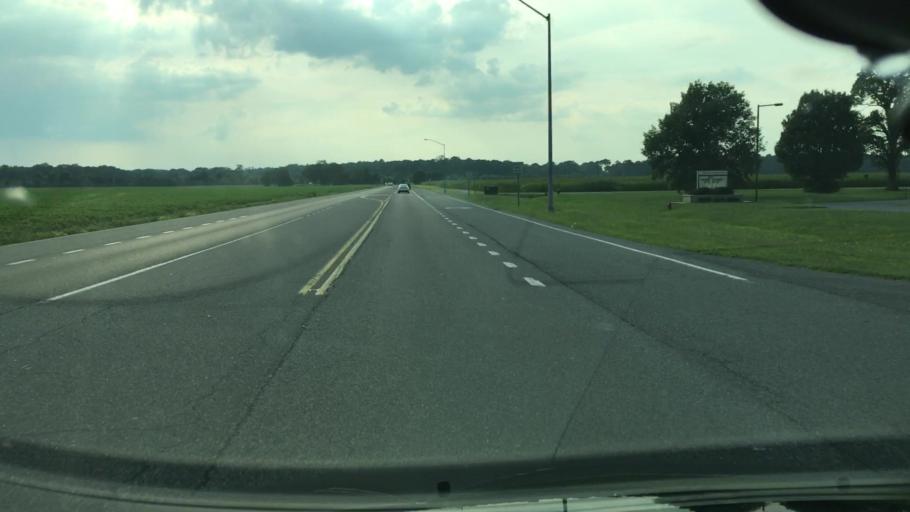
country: US
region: Maryland
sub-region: Worcester County
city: Ocean Pines
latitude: 38.3894
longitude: -75.1928
